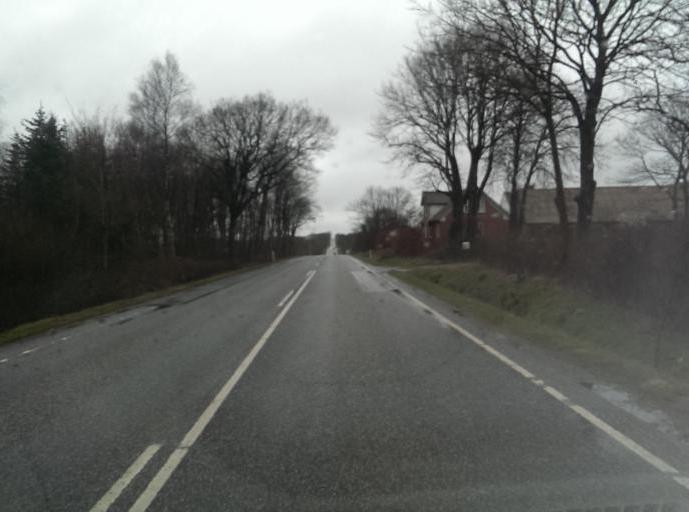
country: DK
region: Central Jutland
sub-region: Ringkobing-Skjern Kommune
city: Skjern
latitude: 56.0401
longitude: 8.4065
